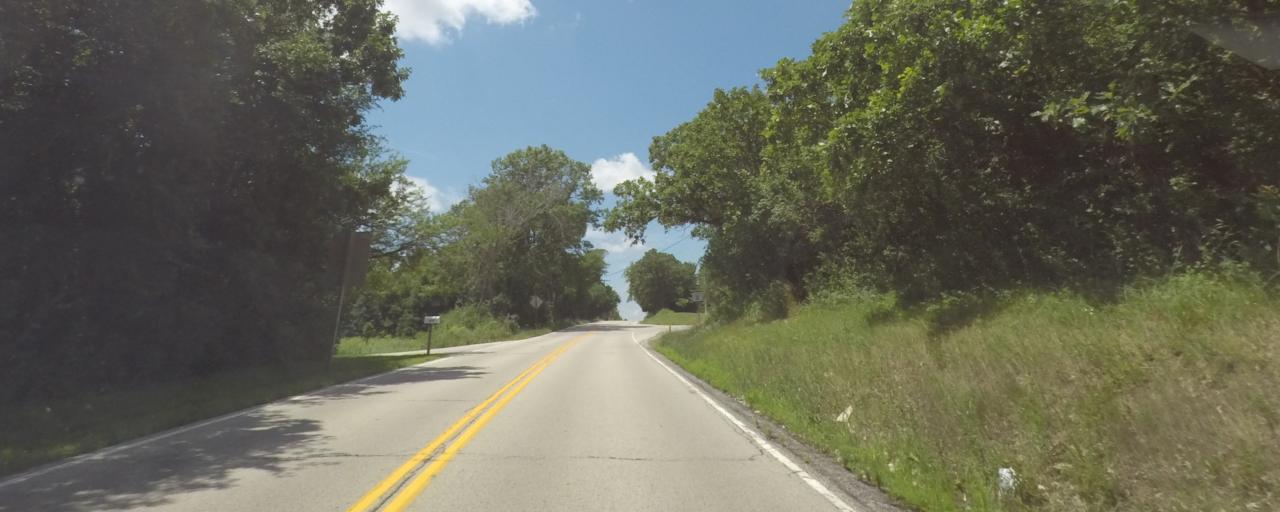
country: US
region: Wisconsin
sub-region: Waukesha County
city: Wales
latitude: 42.9955
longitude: -88.3856
